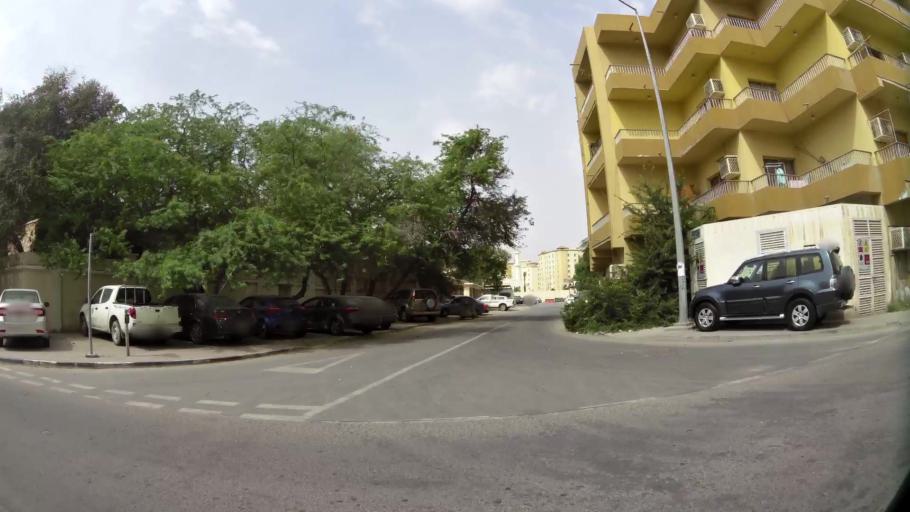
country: QA
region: Baladiyat ad Dawhah
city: Doha
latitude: 25.2840
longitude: 51.5012
